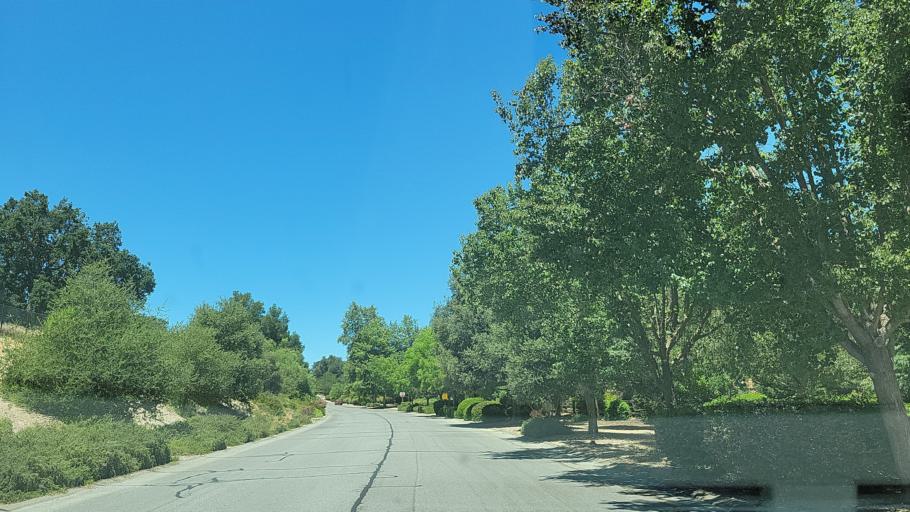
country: US
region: California
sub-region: San Luis Obispo County
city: Atascadero
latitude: 35.5137
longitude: -120.6744
